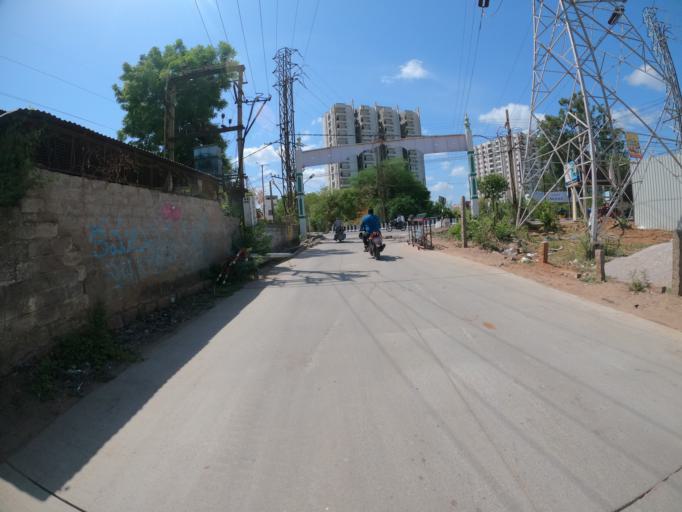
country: IN
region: Telangana
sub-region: Hyderabad
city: Hyderabad
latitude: 17.3574
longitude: 78.3832
